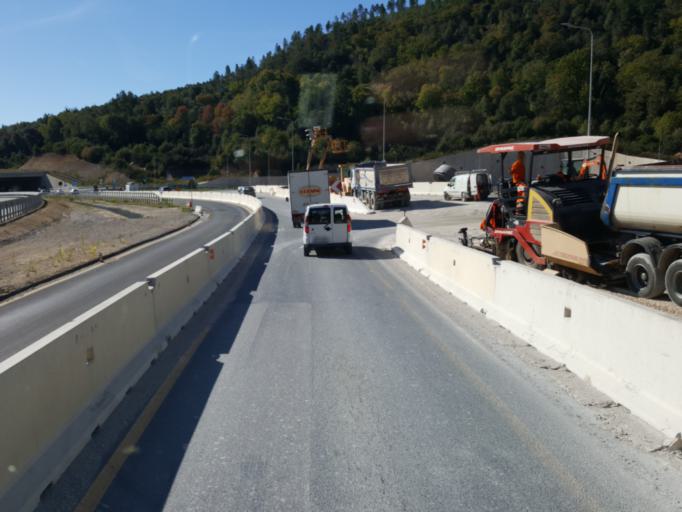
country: IT
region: Tuscany
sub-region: Provincia di Grosseto
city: Civitella Marittima
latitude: 43.0671
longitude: 11.2945
